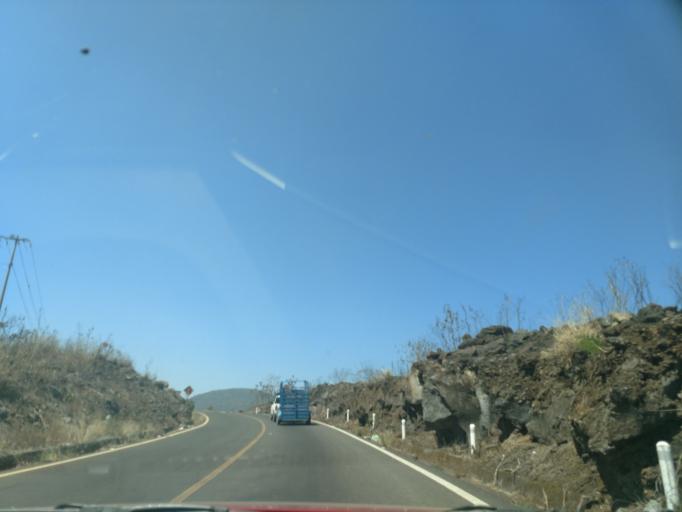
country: MX
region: Nayarit
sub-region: Tepic
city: La Corregidora
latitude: 21.5005
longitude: -104.7573
